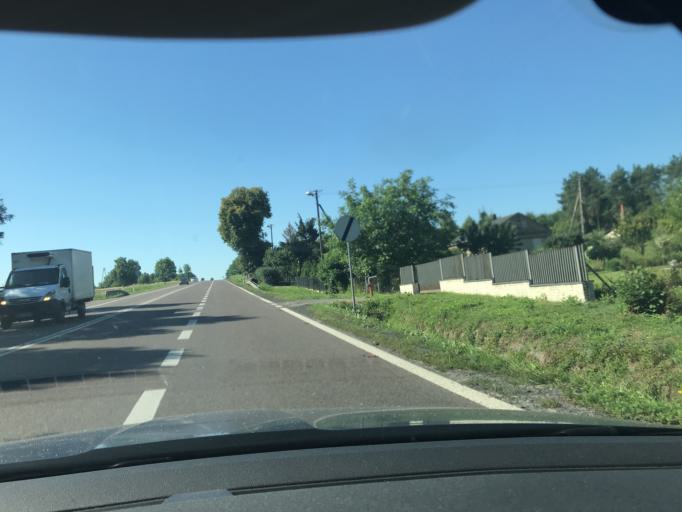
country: PL
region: Lublin Voivodeship
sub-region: Powiat krasnostawski
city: Izbica
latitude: 50.8840
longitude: 23.1501
